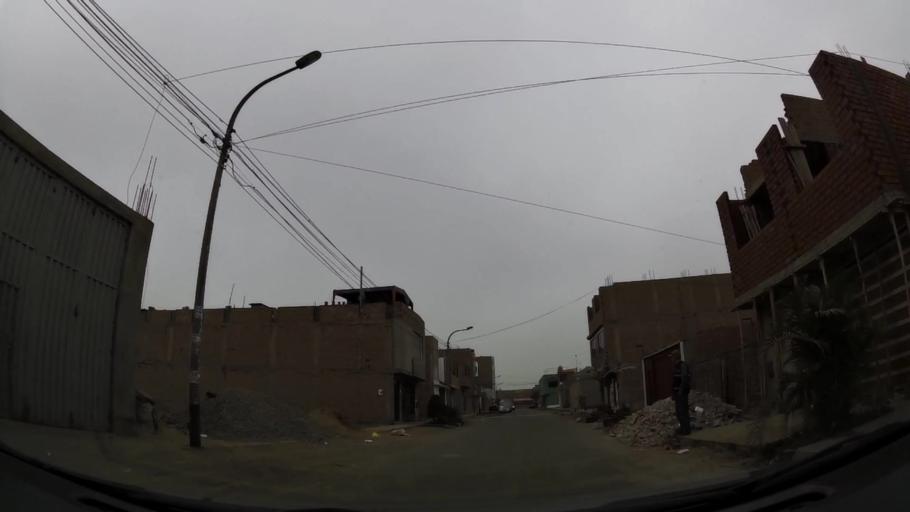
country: PE
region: Lima
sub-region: Lima
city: Urb. Santo Domingo
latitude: -11.8864
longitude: -77.0406
